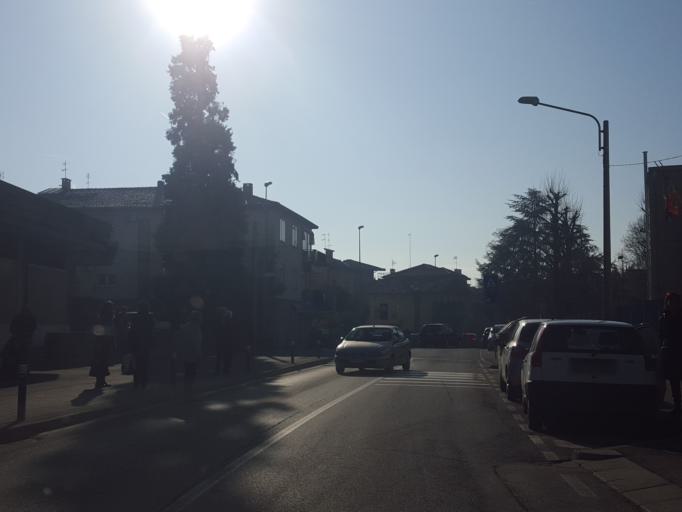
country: IT
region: Veneto
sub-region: Provincia di Vicenza
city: Vicenza
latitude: 45.5459
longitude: 11.5680
